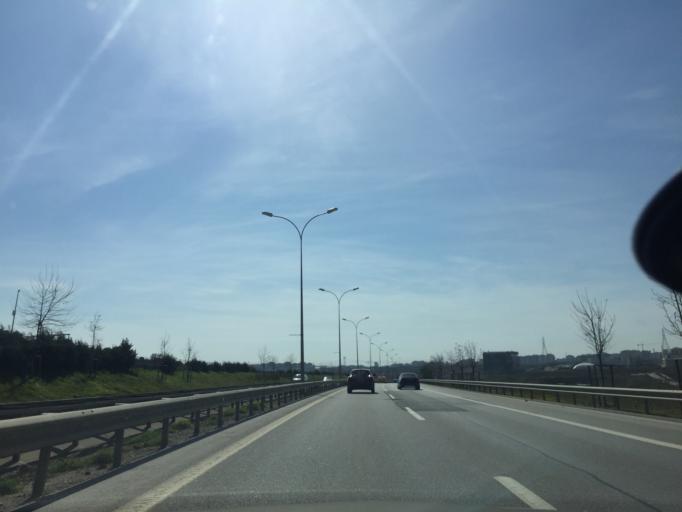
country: TR
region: Istanbul
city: Sultanbeyli
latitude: 40.9253
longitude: 29.3251
